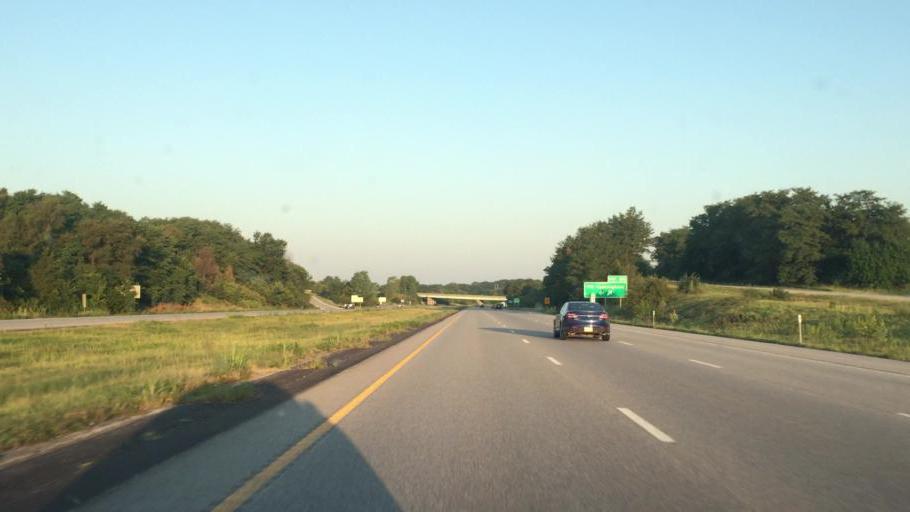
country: US
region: Missouri
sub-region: Clay County
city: Smithville
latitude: 39.3083
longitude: -94.5943
